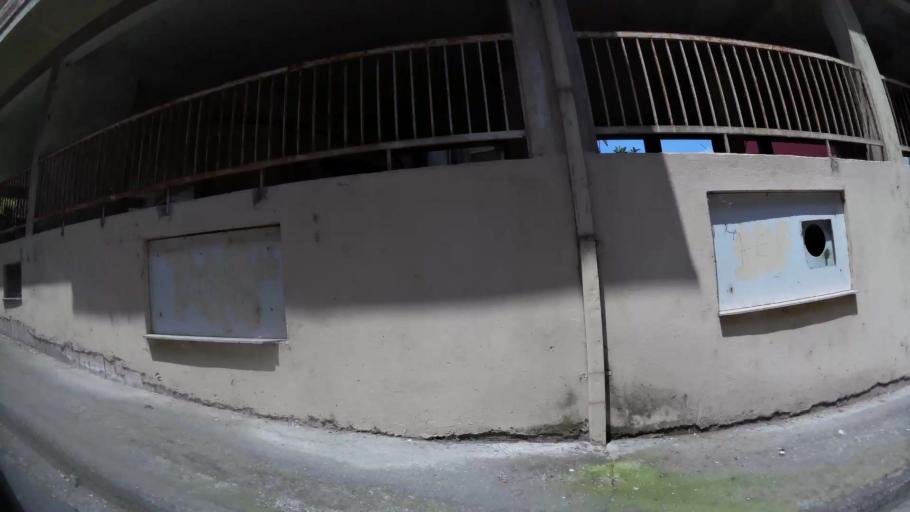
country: GR
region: Central Macedonia
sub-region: Nomos Imathias
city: Veroia
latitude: 40.5181
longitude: 22.1989
